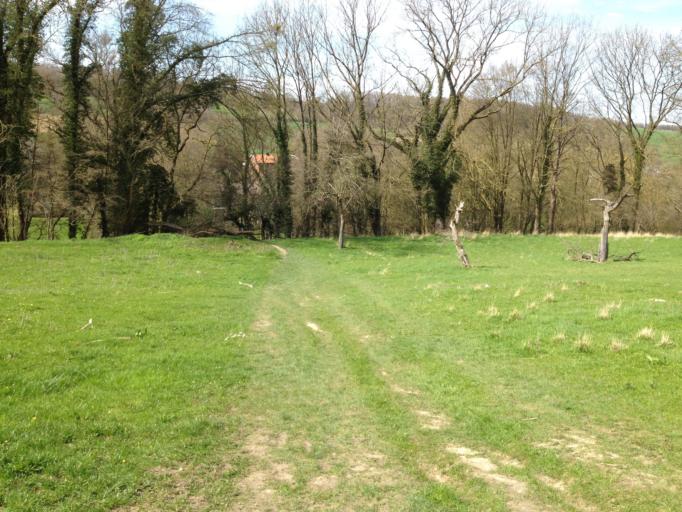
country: BE
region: Flanders
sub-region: Provincie Limburg
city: Sint-Pieters-Voeren
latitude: 50.7801
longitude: 5.8580
